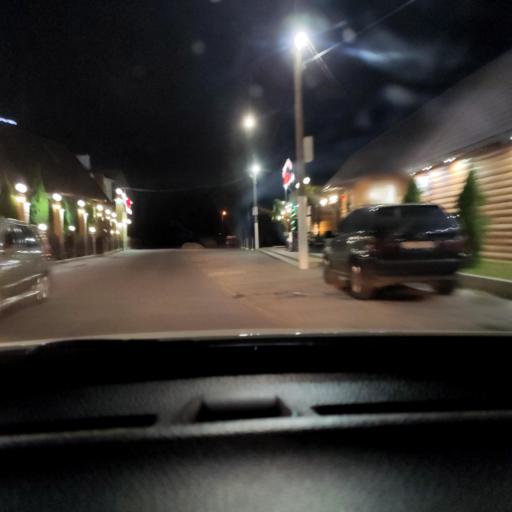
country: RU
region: Voronezj
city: Somovo
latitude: 51.6771
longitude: 39.3313
